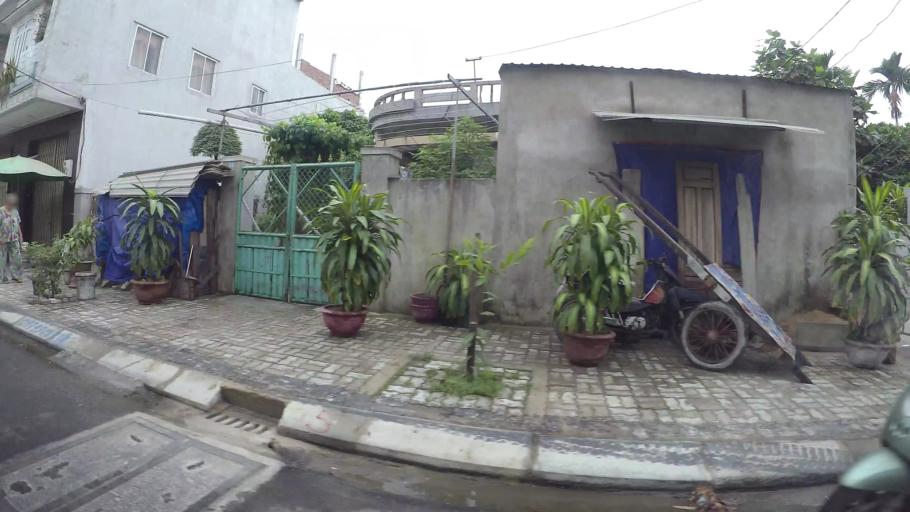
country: VN
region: Da Nang
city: Son Tra
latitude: 16.0856
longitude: 108.2416
